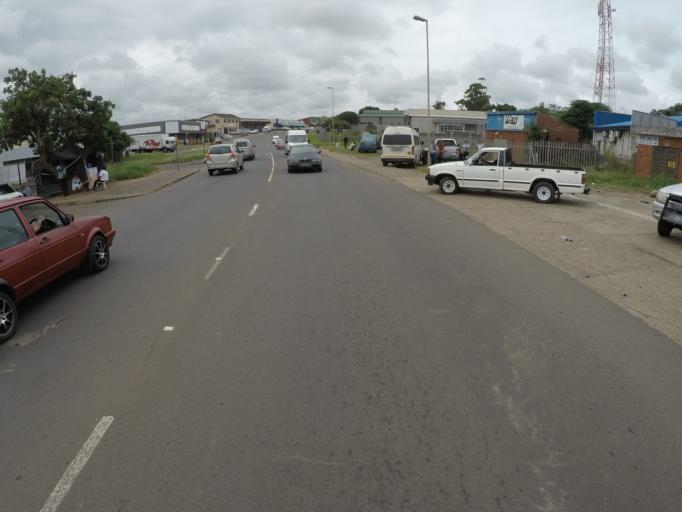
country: ZA
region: KwaZulu-Natal
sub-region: uThungulu District Municipality
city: Empangeni
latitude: -28.7699
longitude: 31.9057
